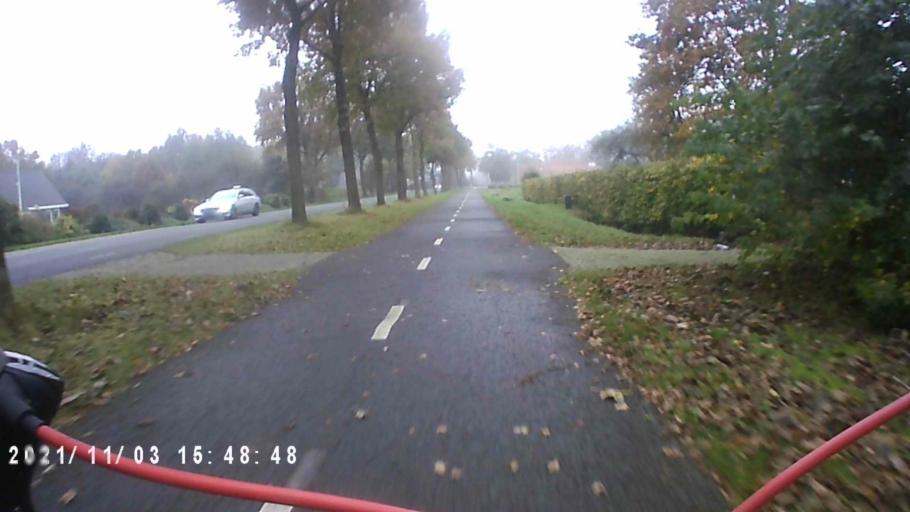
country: NL
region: Groningen
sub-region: Gemeente Leek
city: Leek
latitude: 53.0861
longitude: 6.3387
